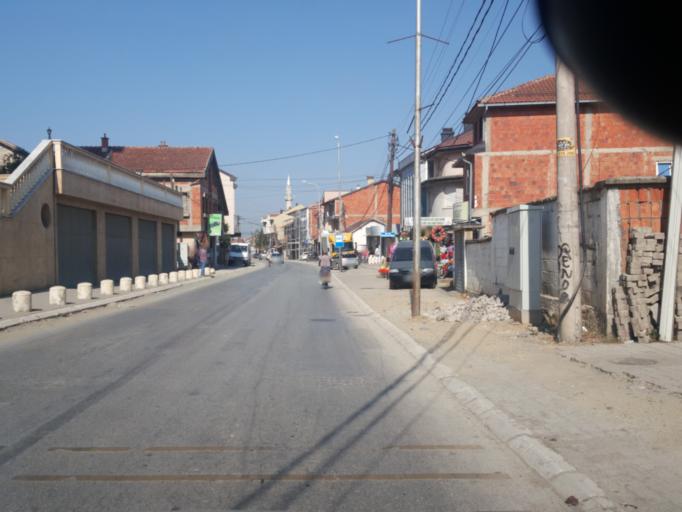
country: XK
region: Gjakova
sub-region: Komuna e Gjakoves
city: Gjakove
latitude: 42.3733
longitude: 20.4241
